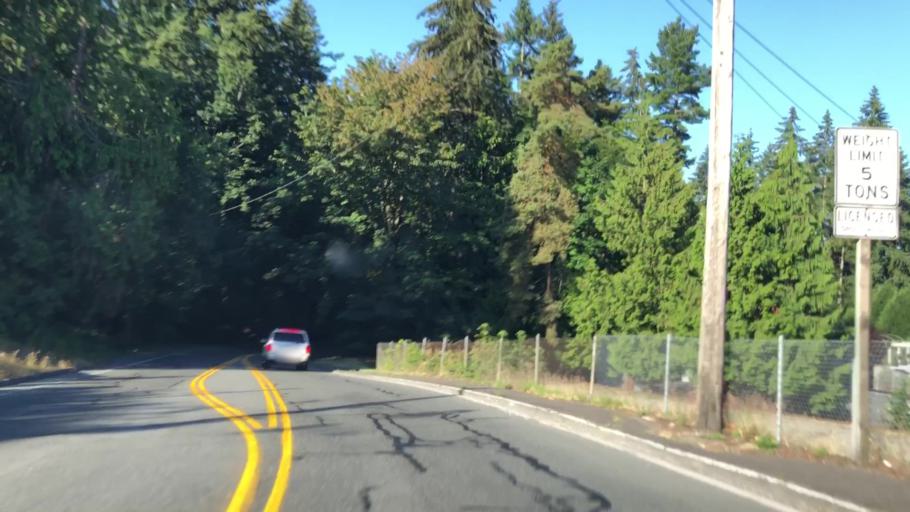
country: US
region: Washington
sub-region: Snohomish County
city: Edmonds
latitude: 47.8212
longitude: -122.3526
